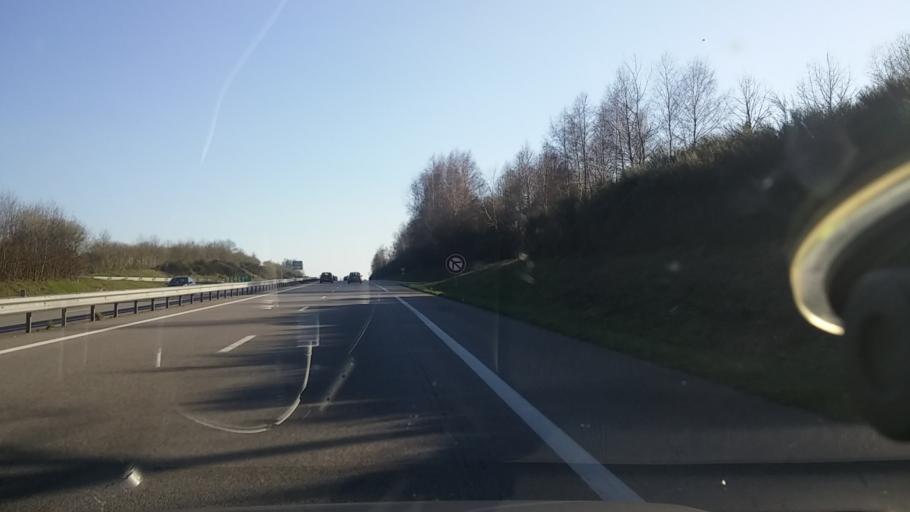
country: FR
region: Limousin
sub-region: Departement de la Haute-Vienne
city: Saint-Sulpice-les-Feuilles
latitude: 46.3545
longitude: 1.4269
